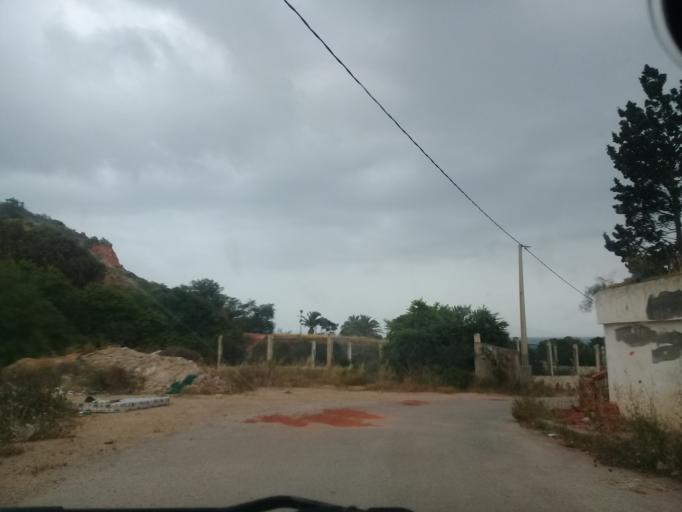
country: TN
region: Tunis
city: Sidi Bou Said
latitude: 36.8654
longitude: 10.3411
